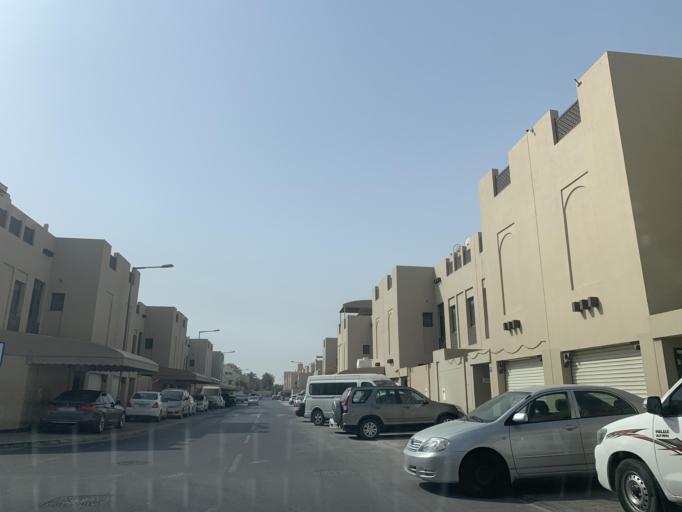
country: BH
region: Northern
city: Madinat `Isa
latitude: 26.1867
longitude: 50.5608
